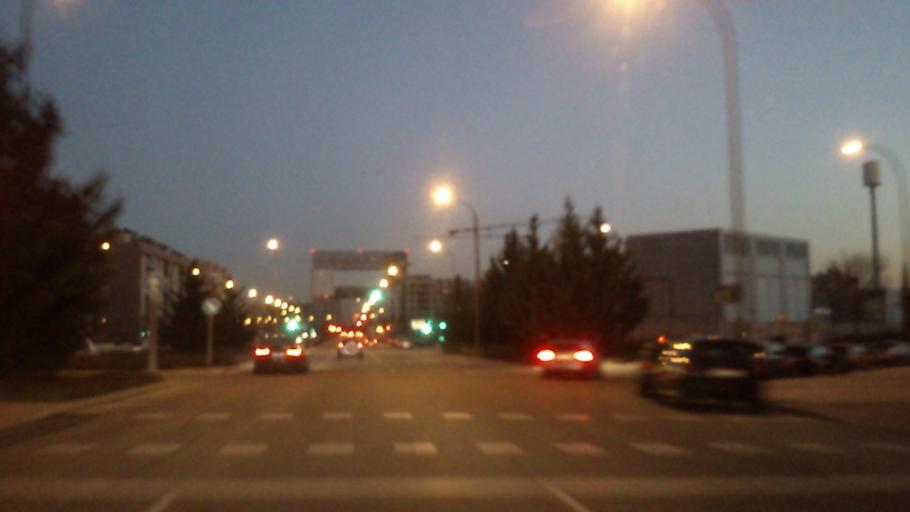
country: ES
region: Madrid
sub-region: Provincia de Madrid
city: Pinar de Chamartin
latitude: 40.4918
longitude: -3.6615
